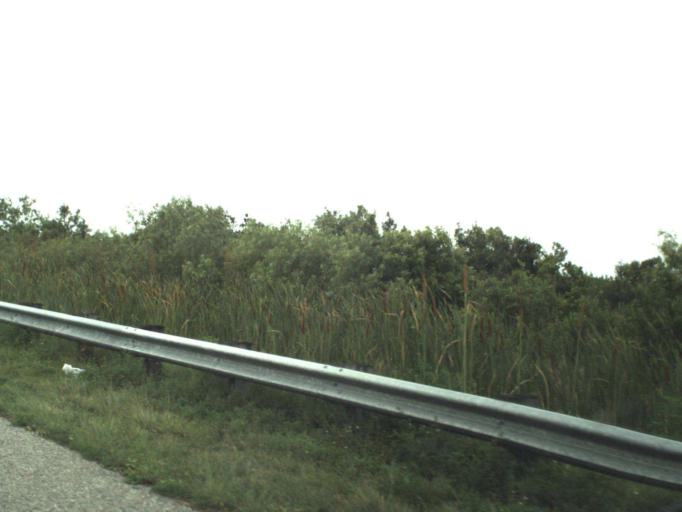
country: US
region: Florida
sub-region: Brevard County
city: Titusville
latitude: 28.5508
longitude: -80.8654
